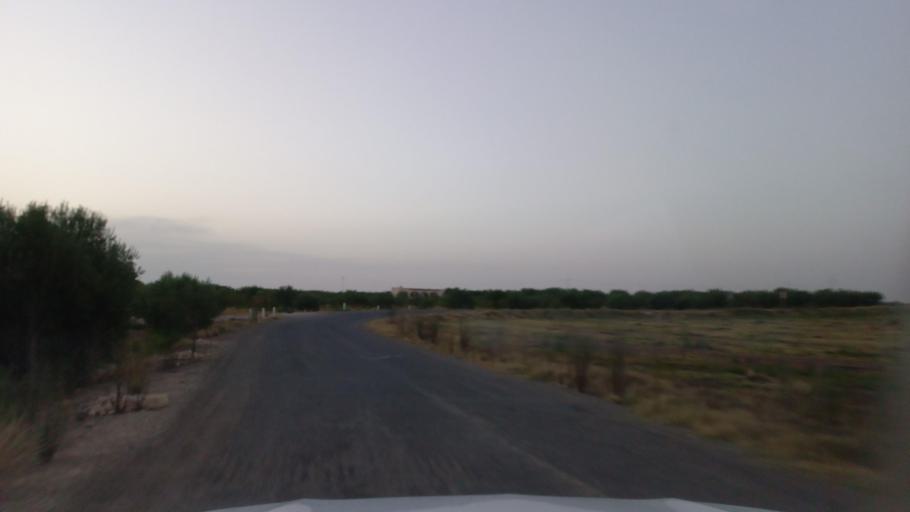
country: TN
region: Al Qasrayn
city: Kasserine
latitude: 35.2695
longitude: 9.0302
